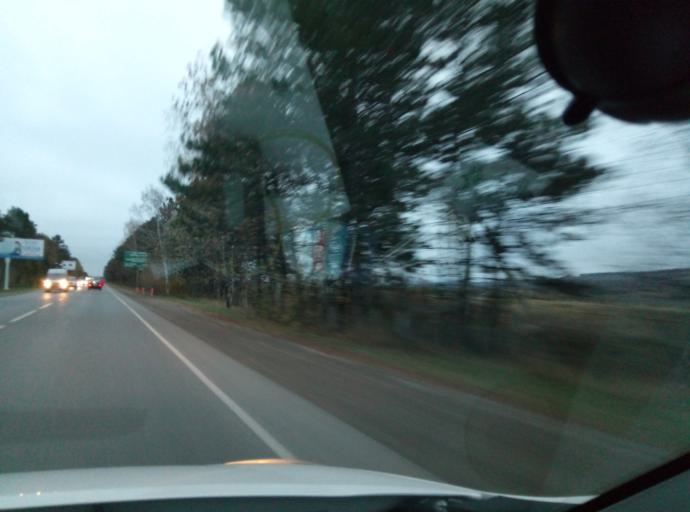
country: RU
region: Stavropol'skiy
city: Vinsady
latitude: 44.0547
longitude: 42.9340
